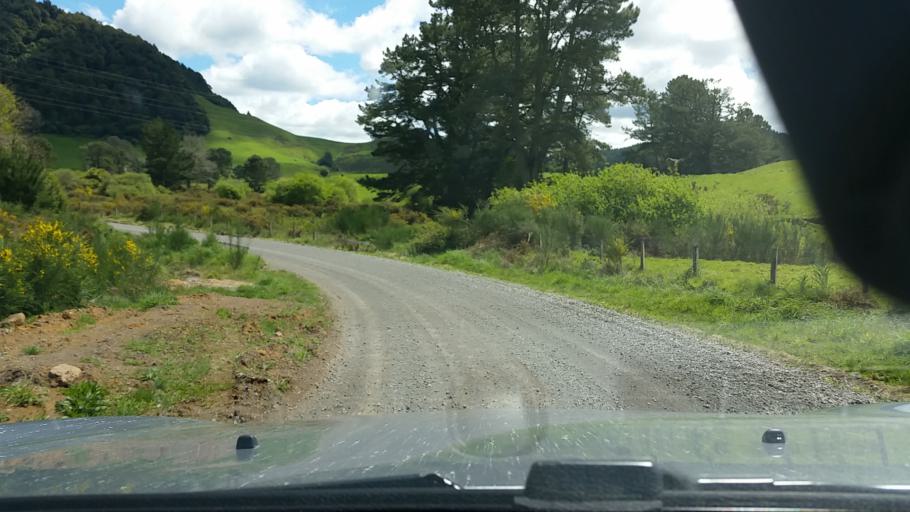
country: NZ
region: Bay of Plenty
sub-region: Rotorua District
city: Rotorua
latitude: -38.2352
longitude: 176.1651
